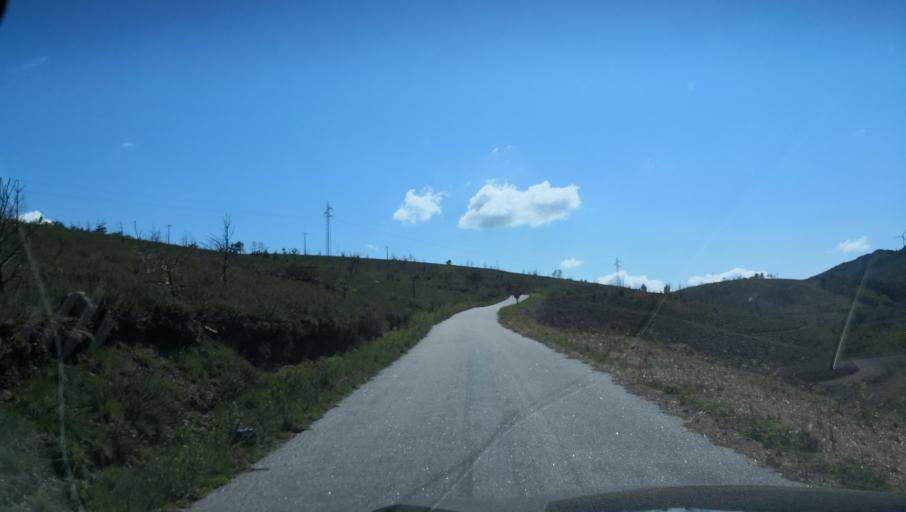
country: PT
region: Vila Real
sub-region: Mesao Frio
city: Mesao Frio
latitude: 41.2865
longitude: -7.9026
